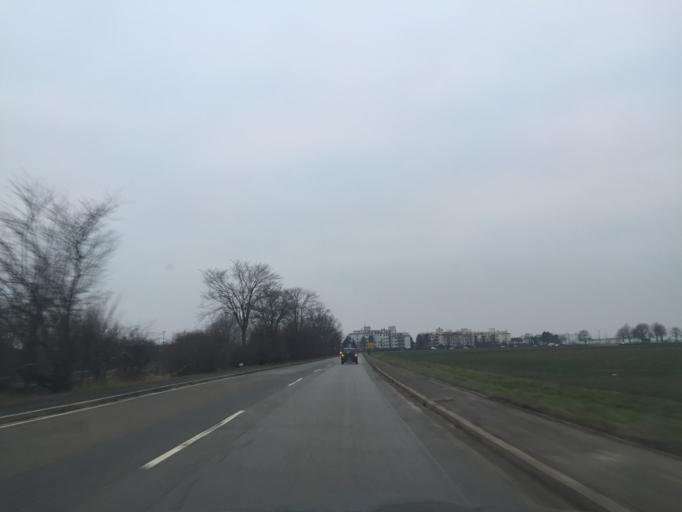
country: DE
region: Baden-Wuerttemberg
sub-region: Karlsruhe Region
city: Heddesheim
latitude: 49.5181
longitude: 8.6110
